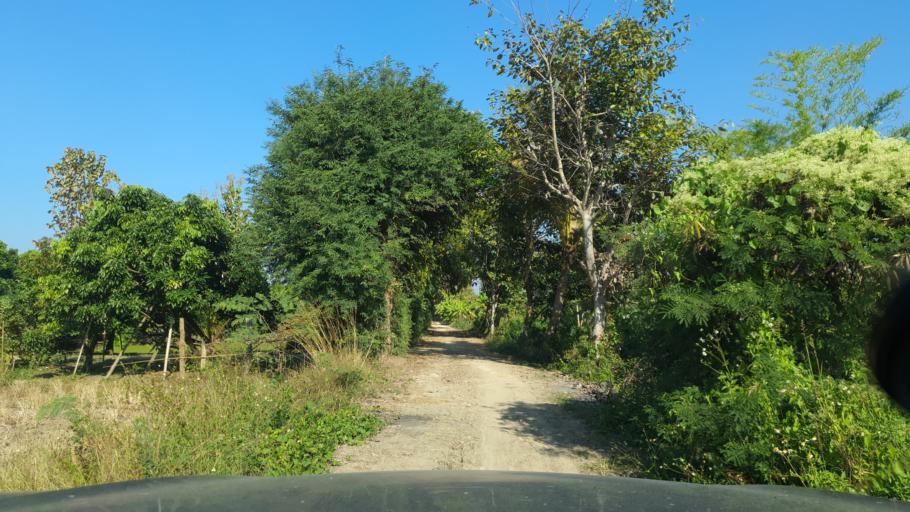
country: TH
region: Chiang Mai
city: Saraphi
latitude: 18.7142
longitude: 99.0762
